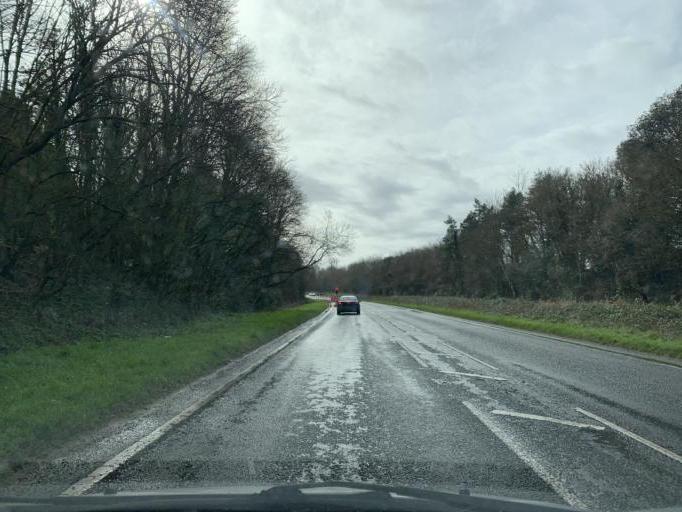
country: GB
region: England
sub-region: Hampshire
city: Fordingbridge
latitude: 50.9324
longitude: -1.7858
